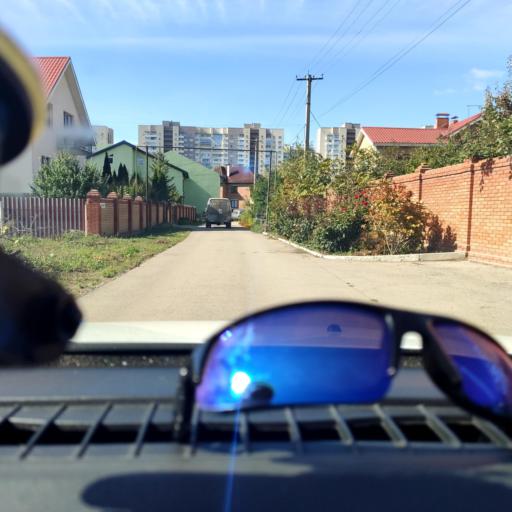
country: RU
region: Samara
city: Samara
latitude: 53.1511
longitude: 50.0806
